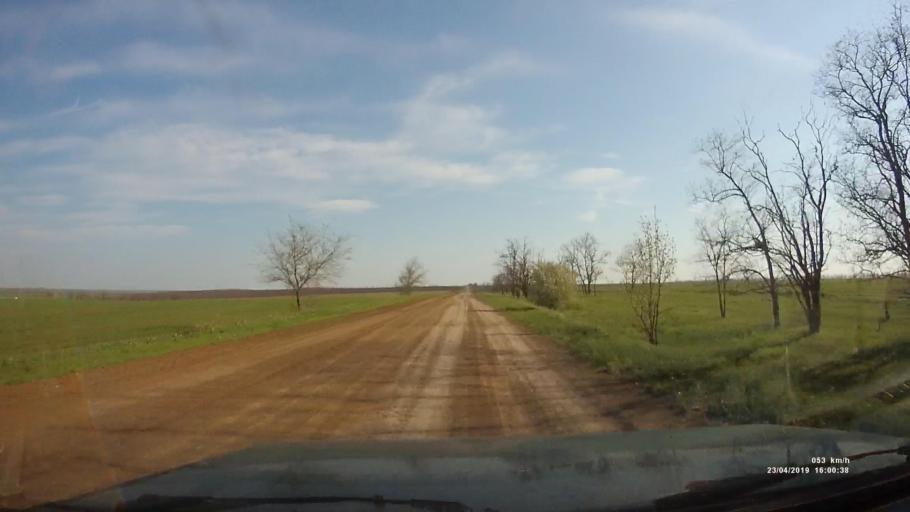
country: RU
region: Rostov
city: Remontnoye
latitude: 46.5078
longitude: 43.1068
